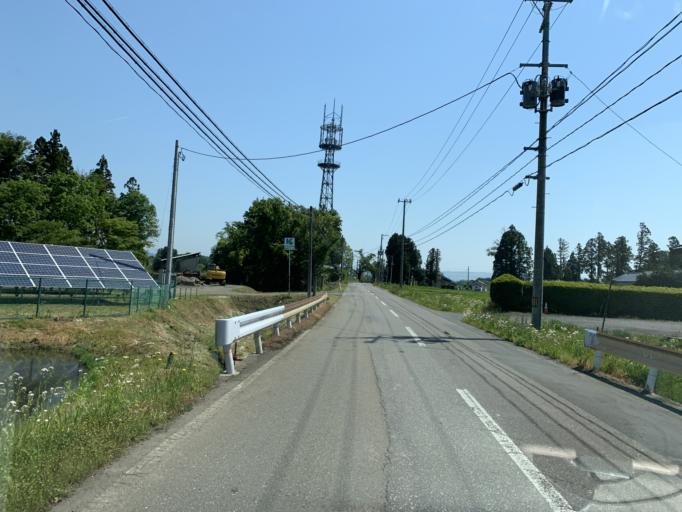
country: JP
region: Iwate
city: Mizusawa
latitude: 39.1826
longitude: 141.0845
